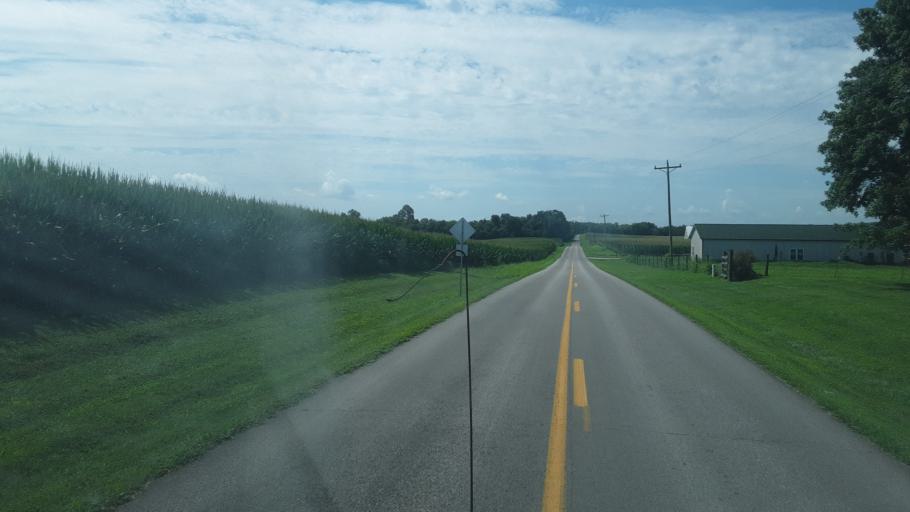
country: US
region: Kentucky
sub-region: Christian County
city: Oak Grove
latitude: 36.7412
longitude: -87.3214
